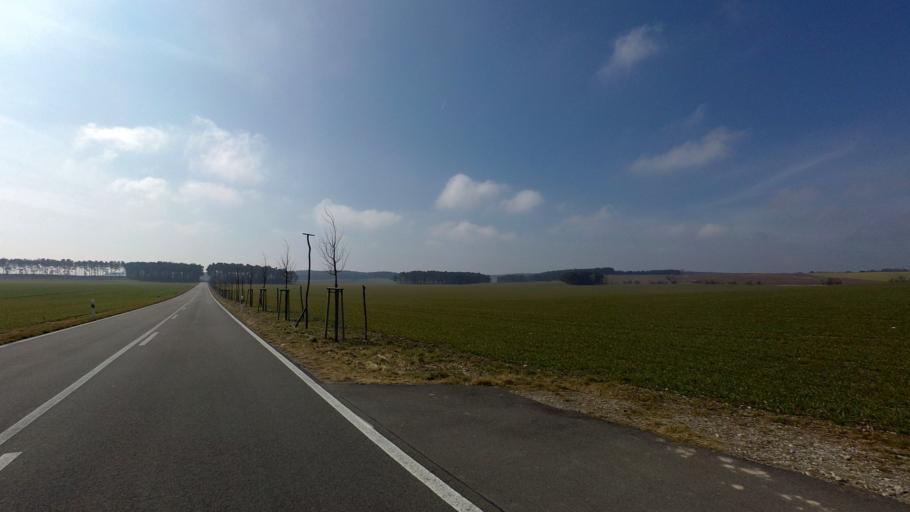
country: DE
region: Brandenburg
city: Belzig
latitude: 52.1258
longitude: 12.6308
